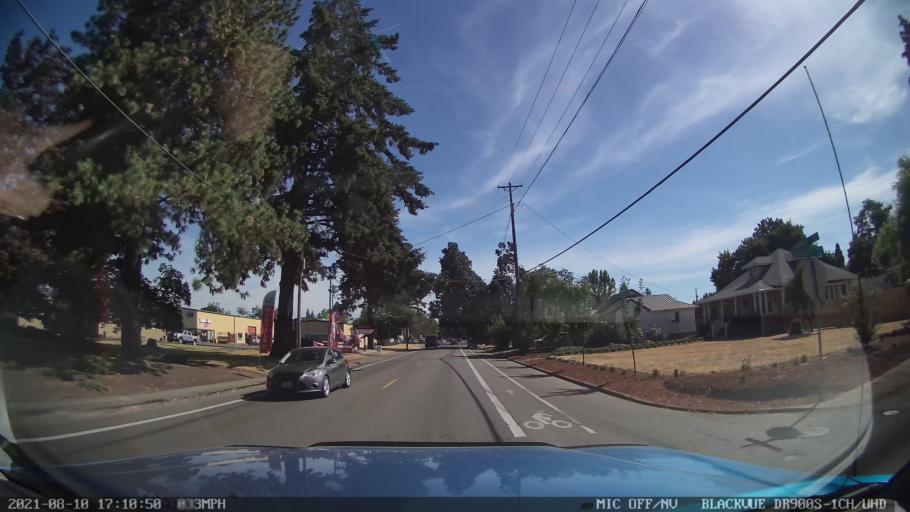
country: US
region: Oregon
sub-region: Marion County
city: Salem
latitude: 44.9643
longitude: -123.0195
